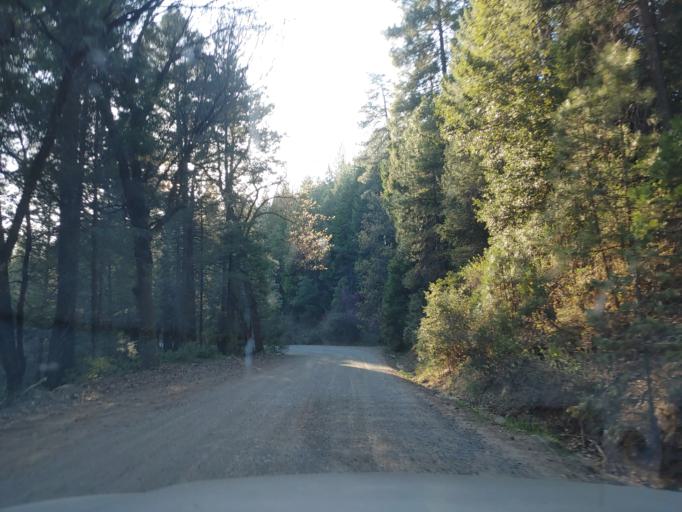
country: US
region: California
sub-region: Shasta County
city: Bella Vista
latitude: 40.8155
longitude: -121.9860
